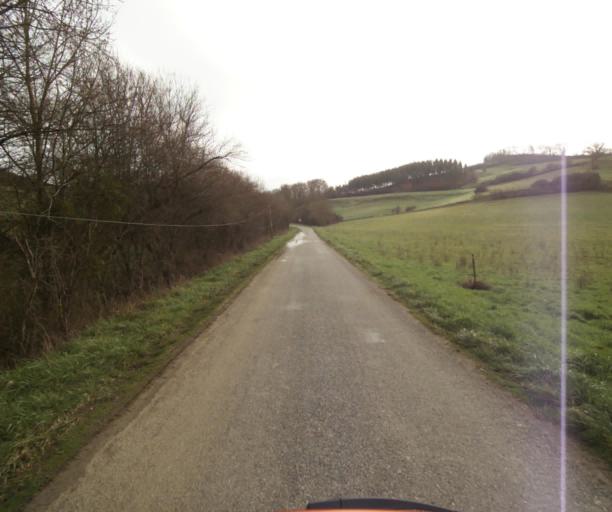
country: FR
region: Midi-Pyrenees
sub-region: Departement de la Haute-Garonne
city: Gaillac-Toulza
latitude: 43.1700
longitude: 1.4980
